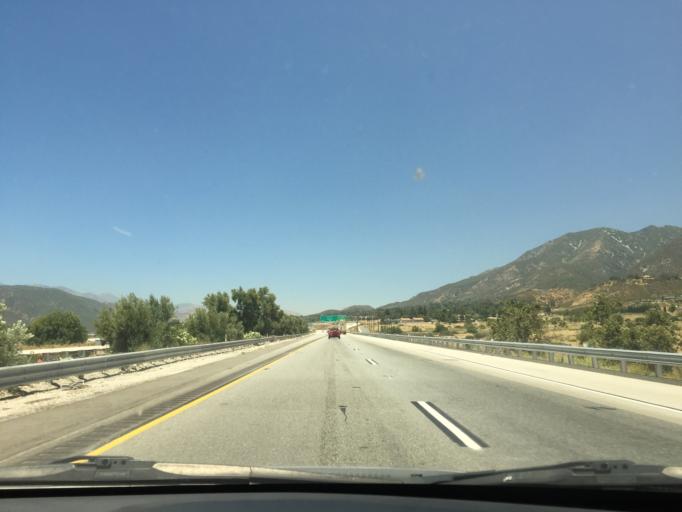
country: US
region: California
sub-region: San Bernardino County
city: Muscoy
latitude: 34.2166
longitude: -117.3944
